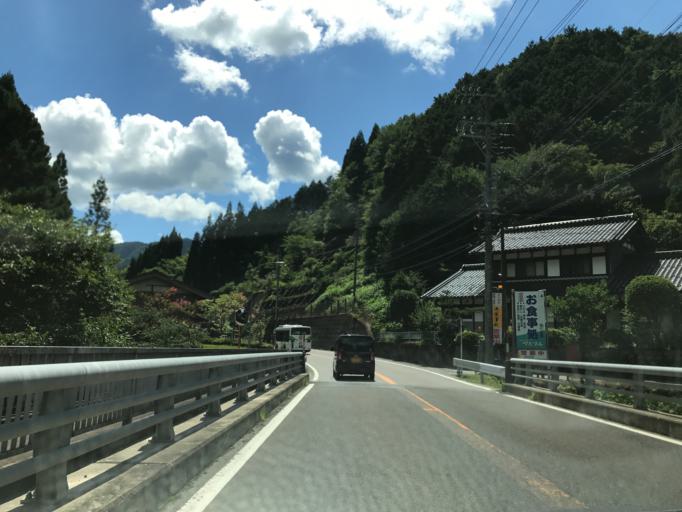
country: JP
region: Gifu
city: Gujo
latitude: 35.8494
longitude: 137.0310
